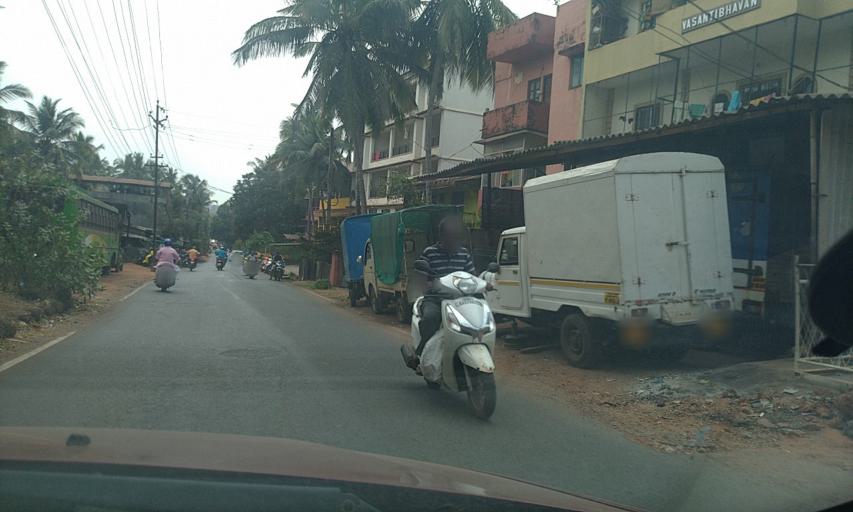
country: IN
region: Goa
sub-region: North Goa
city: Mapuca
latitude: 15.5943
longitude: 73.8005
